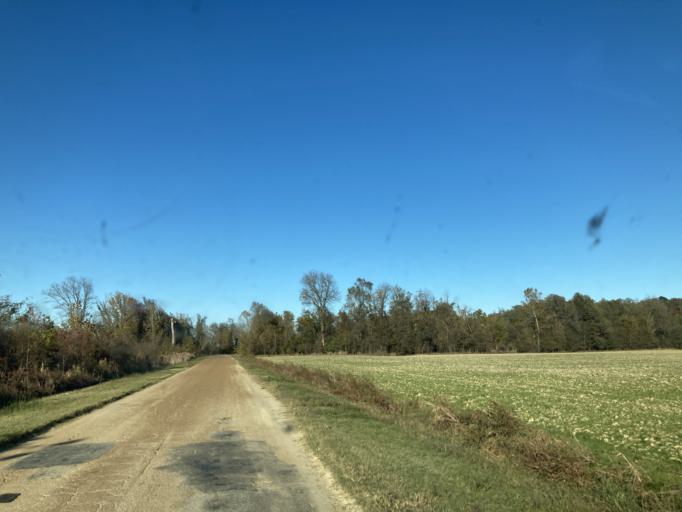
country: US
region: Mississippi
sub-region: Yazoo County
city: Yazoo City
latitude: 32.8118
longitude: -90.4516
